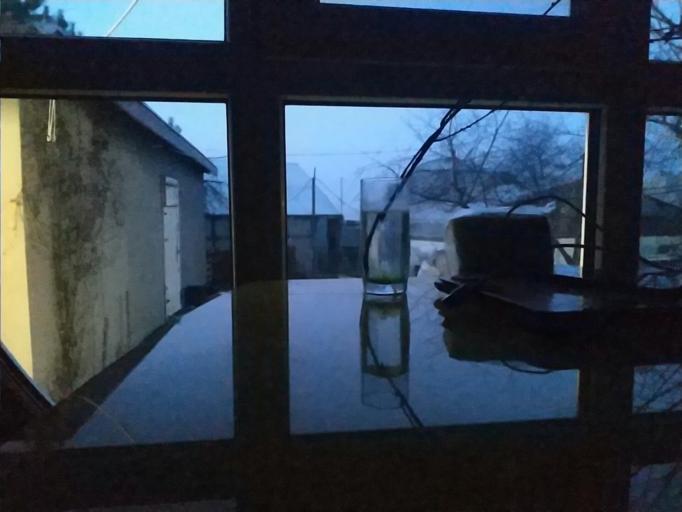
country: RU
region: Republic of Karelia
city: Sukkozero
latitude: 62.8919
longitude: 31.8020
